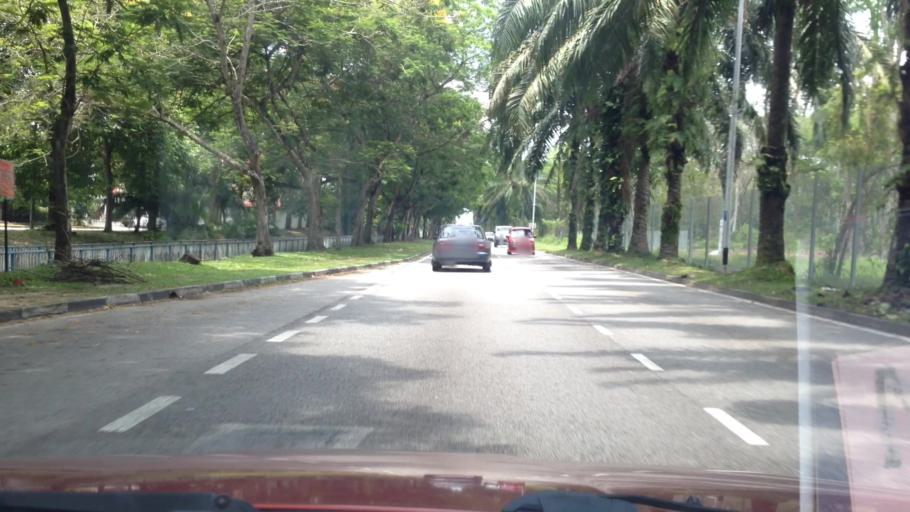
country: MY
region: Selangor
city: Kampung Baru Subang
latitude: 3.1721
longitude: 101.5501
